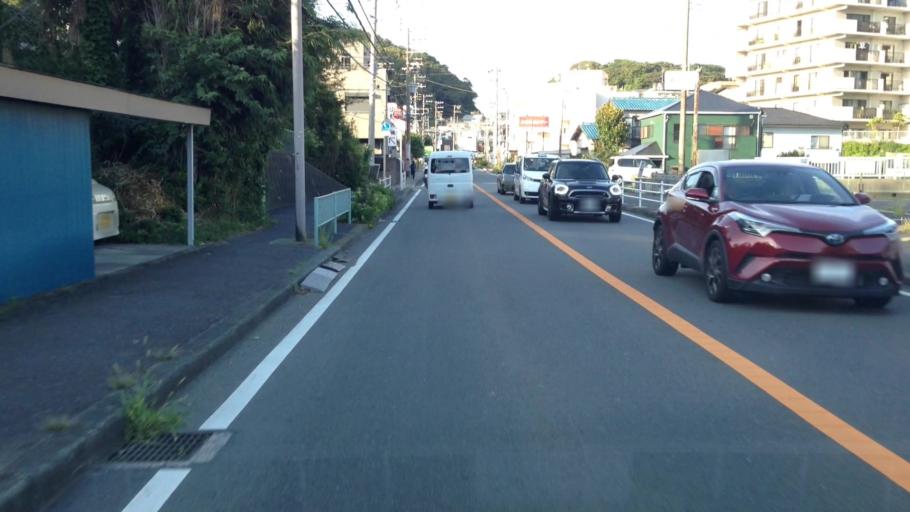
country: JP
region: Kanagawa
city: Yokosuka
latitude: 35.2281
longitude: 139.6514
